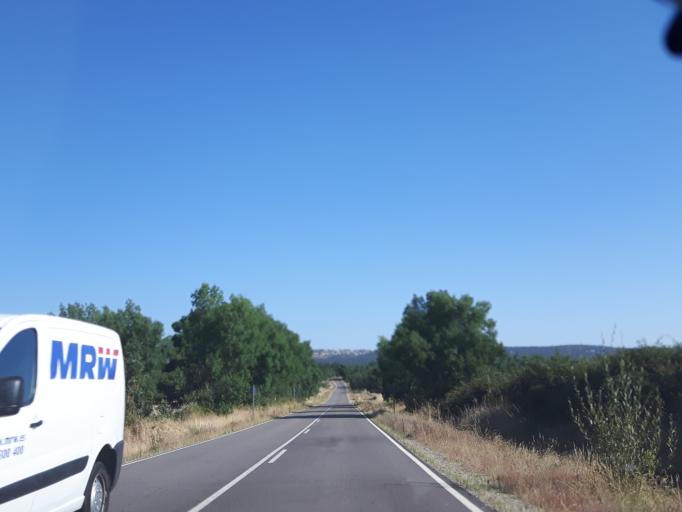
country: ES
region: Castille and Leon
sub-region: Provincia de Salamanca
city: Valdehijaderos
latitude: 40.4216
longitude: -5.8203
